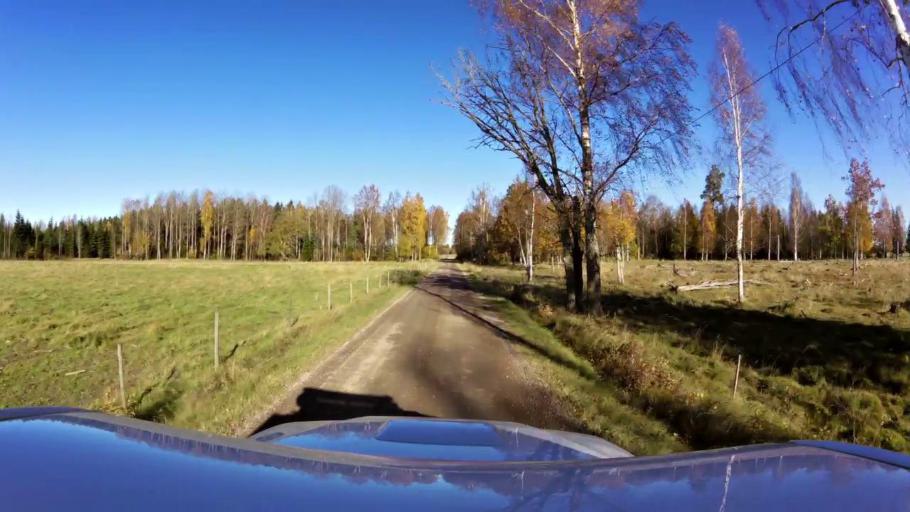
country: SE
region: OEstergoetland
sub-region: Linkopings Kommun
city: Vikingstad
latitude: 58.4870
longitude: 15.3884
